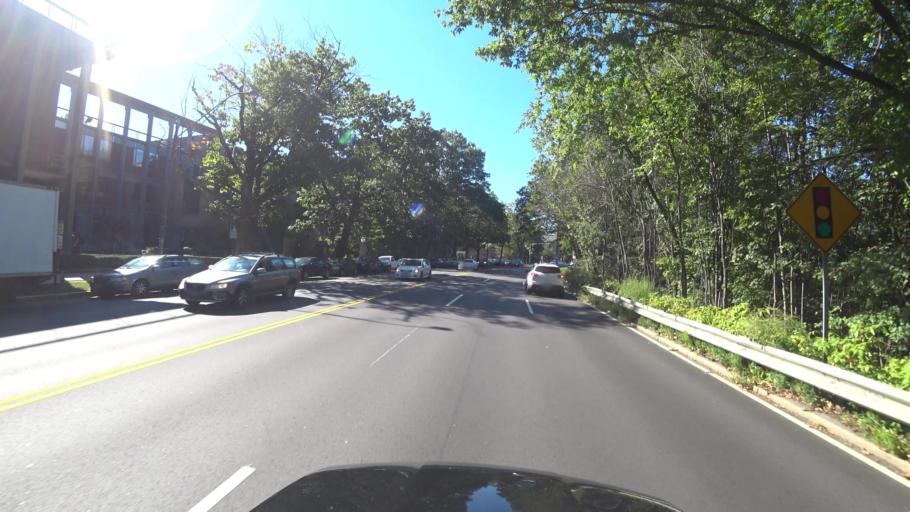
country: US
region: Massachusetts
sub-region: Norfolk County
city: Brookline
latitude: 42.3422
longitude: -71.1066
